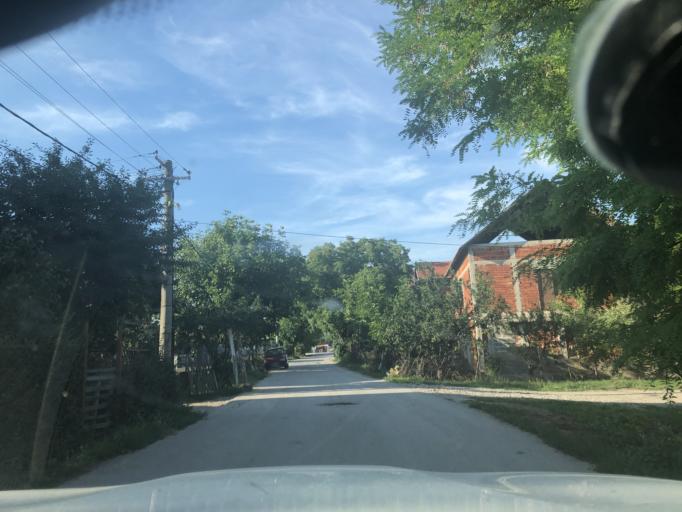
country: RS
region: Central Serbia
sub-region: Nisavski Okrug
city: Nis
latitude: 43.3276
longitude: 21.9558
